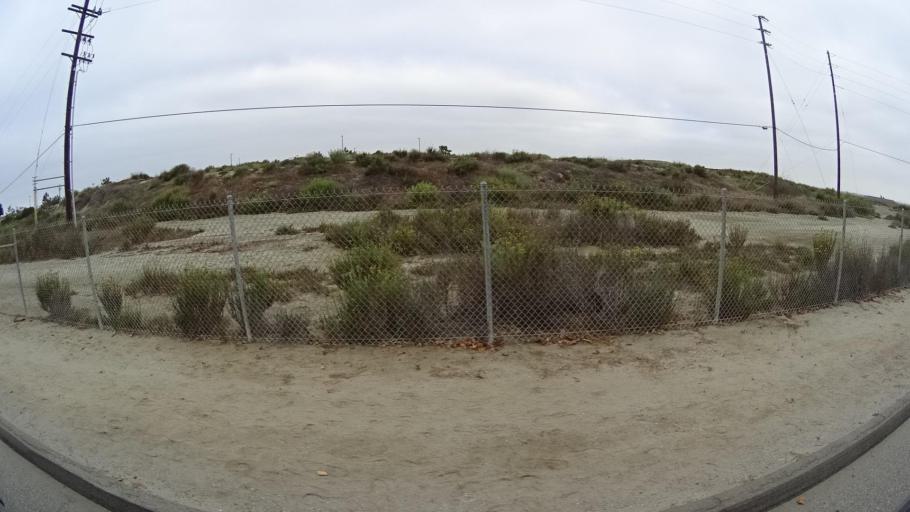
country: US
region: California
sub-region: Orange County
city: Seal Beach
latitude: 33.7291
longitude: -118.0729
